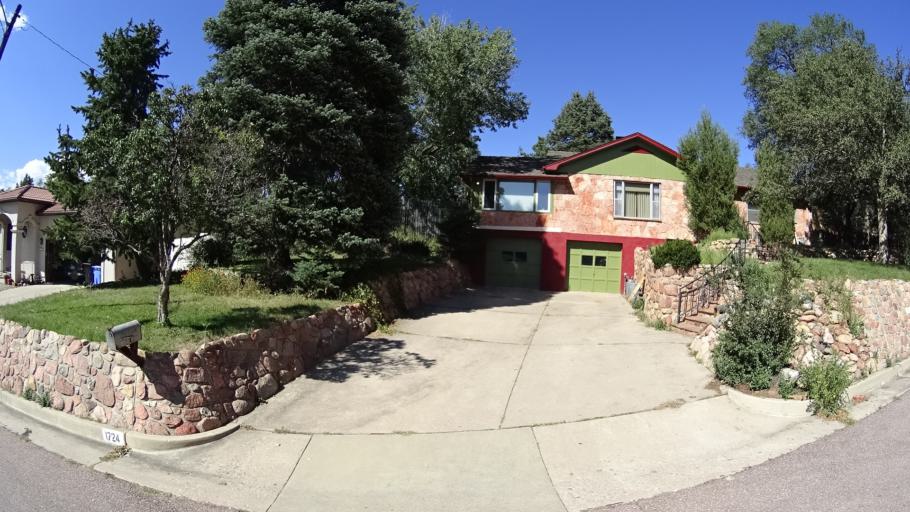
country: US
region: Colorado
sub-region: El Paso County
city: Colorado Springs
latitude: 38.8550
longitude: -104.8468
